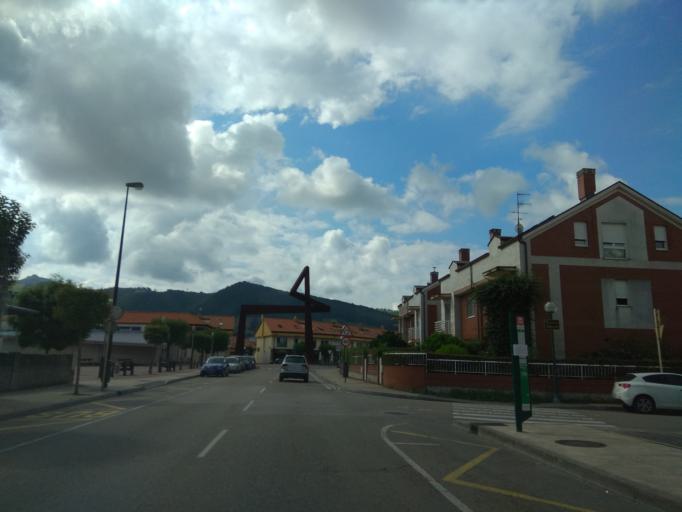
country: ES
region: Cantabria
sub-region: Provincia de Cantabria
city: Torrelavega
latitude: 43.3322
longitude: -4.0436
